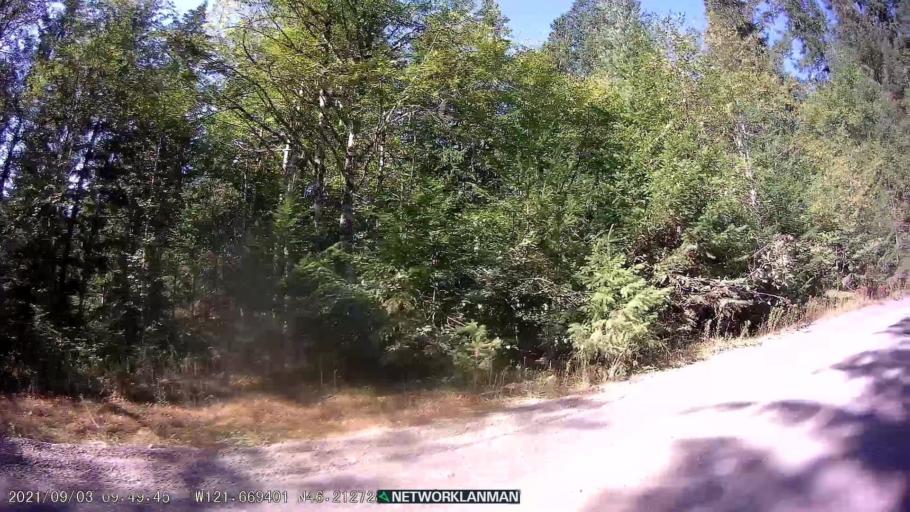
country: US
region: Washington
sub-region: Skamania County
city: Carson
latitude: 46.2172
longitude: -121.6610
